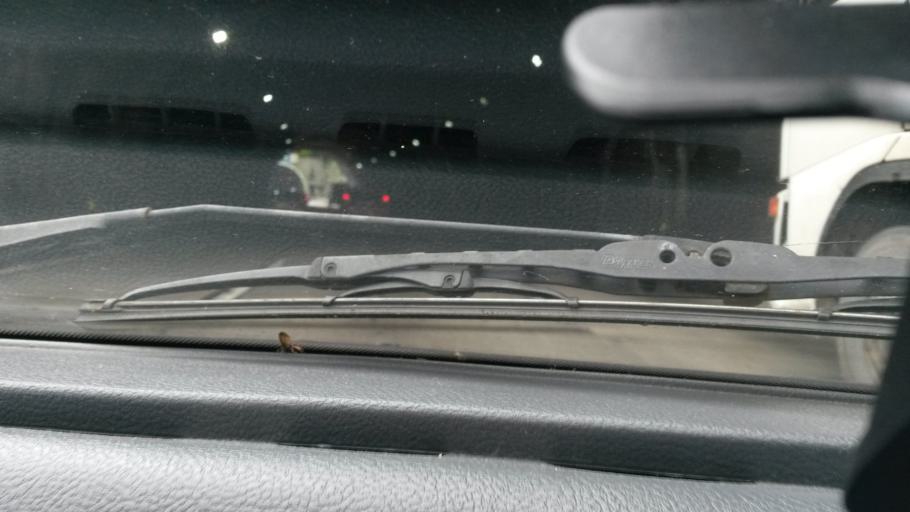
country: BR
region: Sao Paulo
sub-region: Cubatao
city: Cubatao
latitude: -23.9099
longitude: -46.5181
